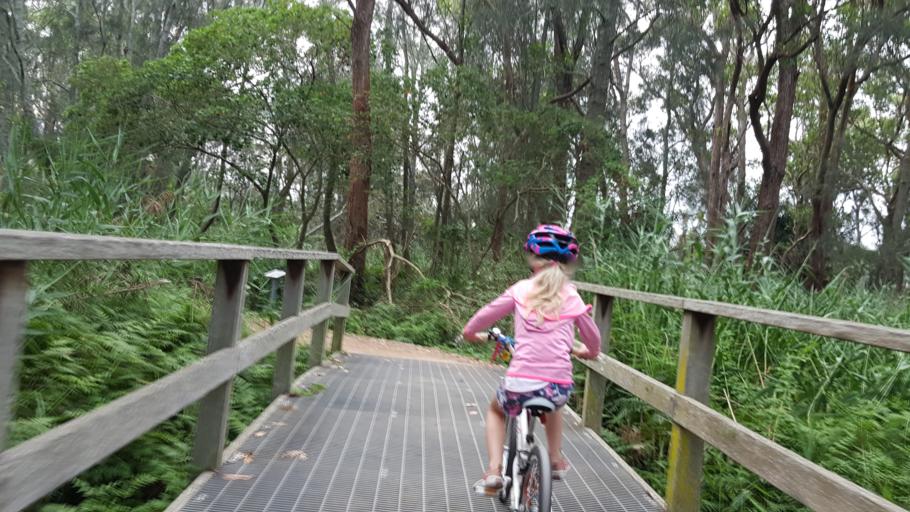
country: AU
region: New South Wales
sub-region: Warringah
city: Narrabeen
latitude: -33.7219
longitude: 151.2774
